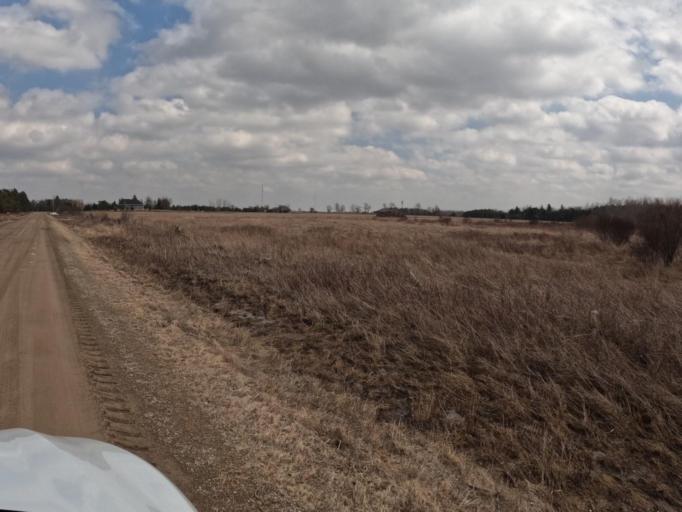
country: CA
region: Ontario
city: Shelburne
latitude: 44.0215
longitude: -80.2927
